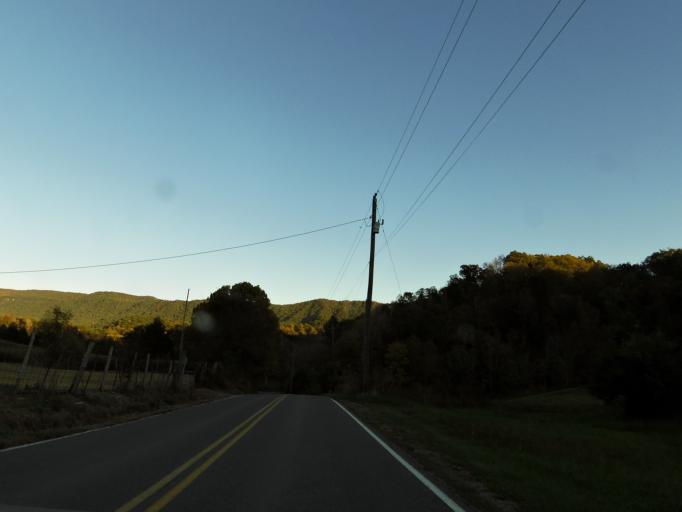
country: US
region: Tennessee
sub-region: Sevier County
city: Seymour
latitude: 35.7997
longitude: -83.7420
